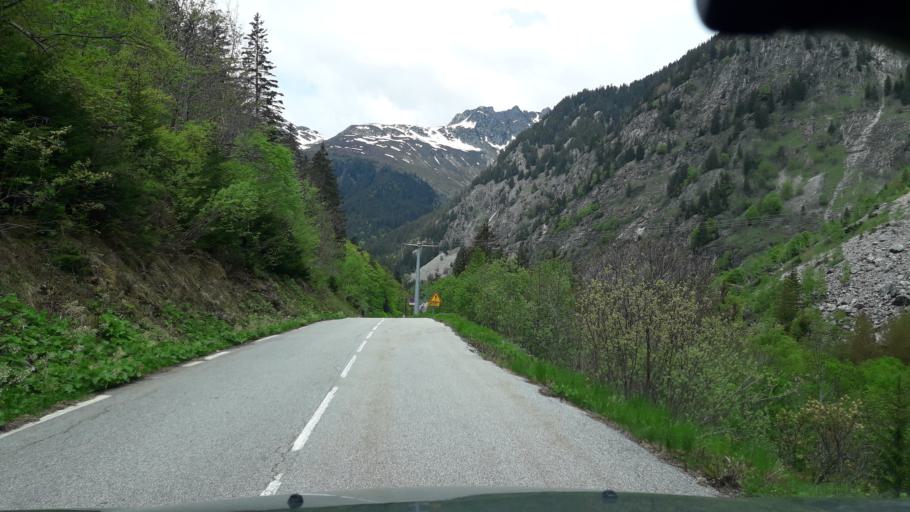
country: FR
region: Rhone-Alpes
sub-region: Departement de l'Isere
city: Theys
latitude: 45.2049
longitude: 6.0710
